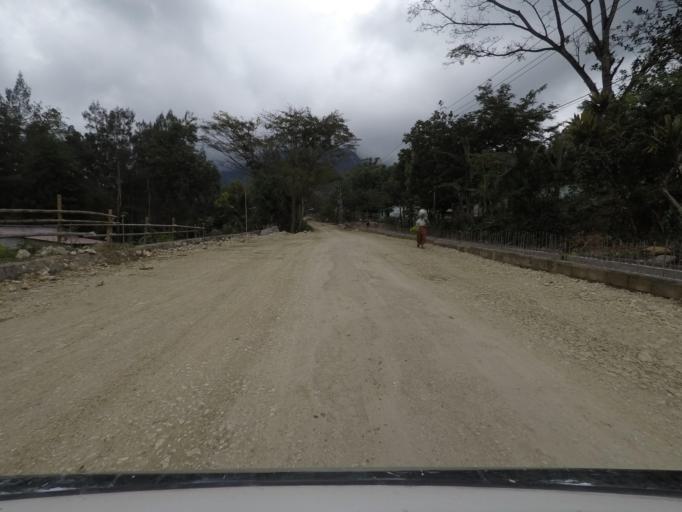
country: TL
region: Baucau
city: Venilale
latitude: -8.7385
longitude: 126.3731
